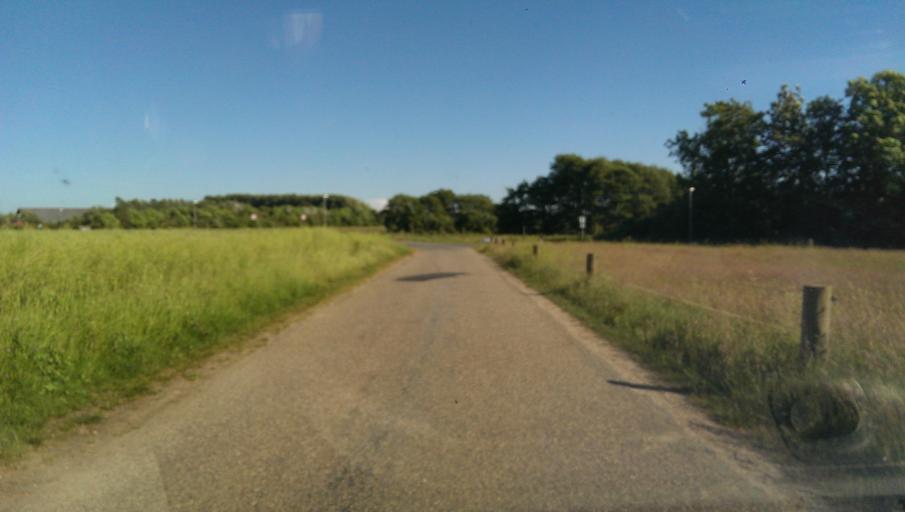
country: DK
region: South Denmark
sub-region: Fano Kommune
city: Nordby
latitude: 55.5220
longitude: 8.3926
